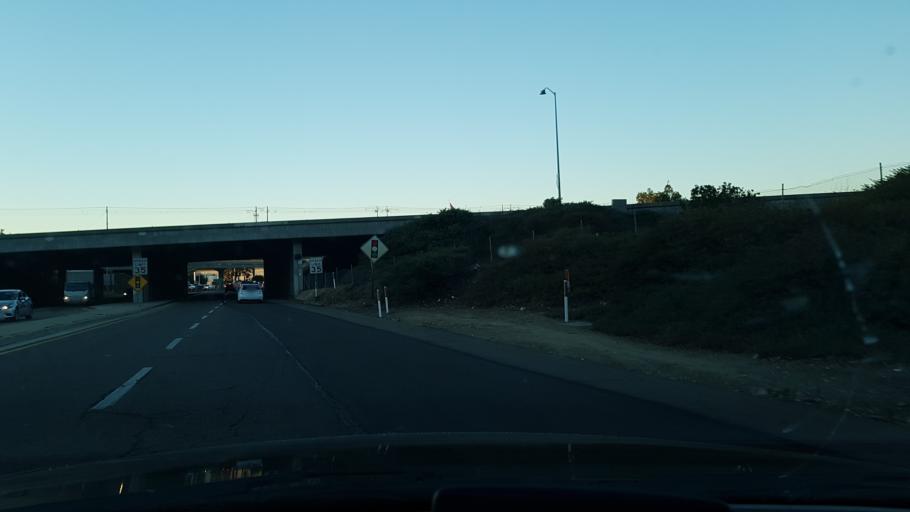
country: US
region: California
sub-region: San Diego County
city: Lemon Grove
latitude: 32.7783
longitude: -117.1007
